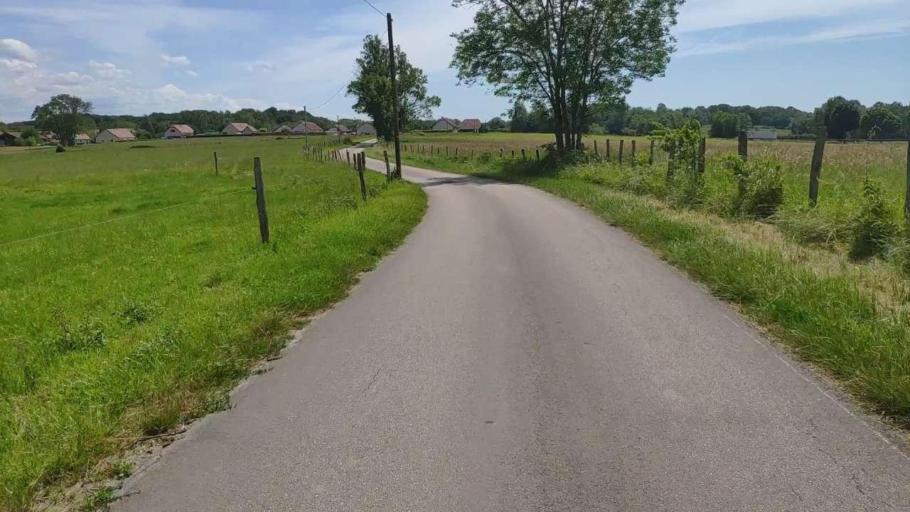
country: FR
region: Franche-Comte
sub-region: Departement du Jura
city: Bletterans
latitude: 46.7695
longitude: 5.4319
